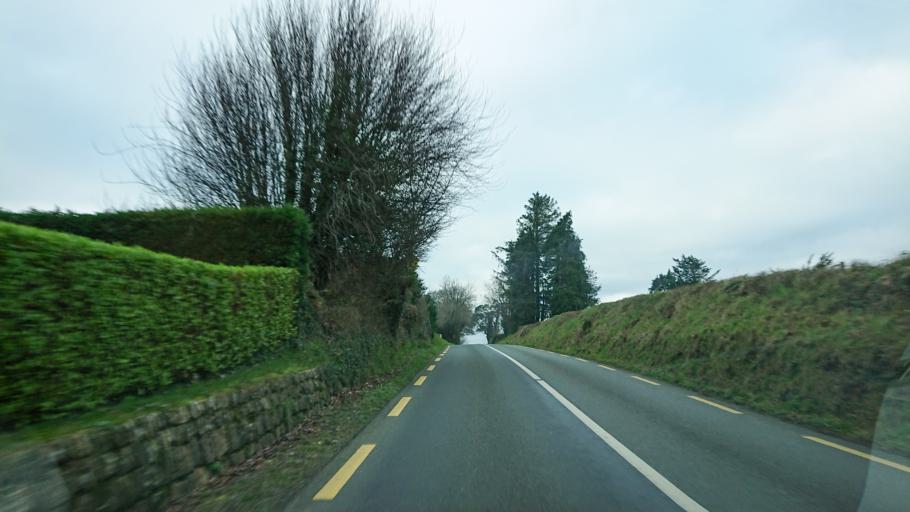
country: IE
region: Munster
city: Carrick-on-Suir
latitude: 52.3014
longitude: -7.4828
